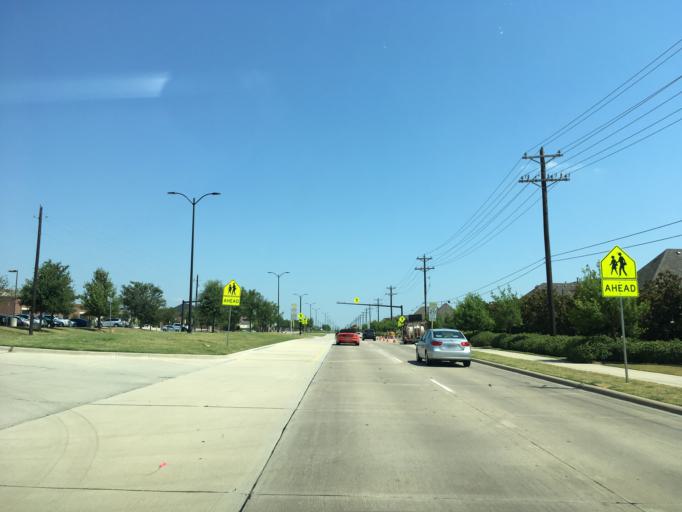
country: US
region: Texas
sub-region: Collin County
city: Frisco
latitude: 33.1769
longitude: -96.7678
